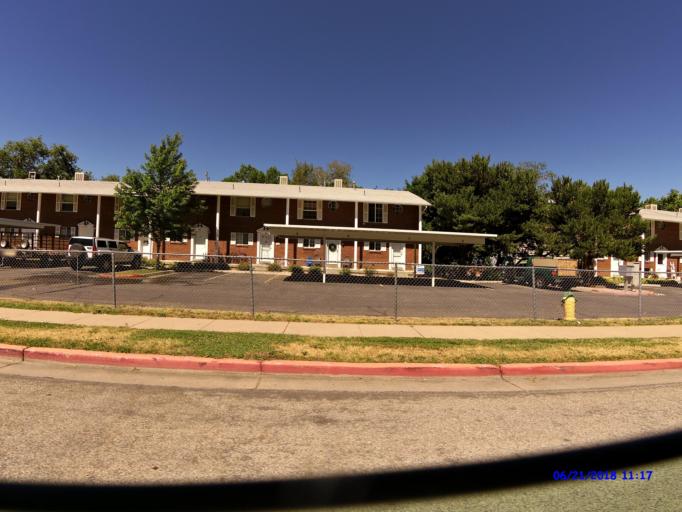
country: US
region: Utah
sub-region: Weber County
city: Ogden
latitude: 41.2563
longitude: -111.9553
